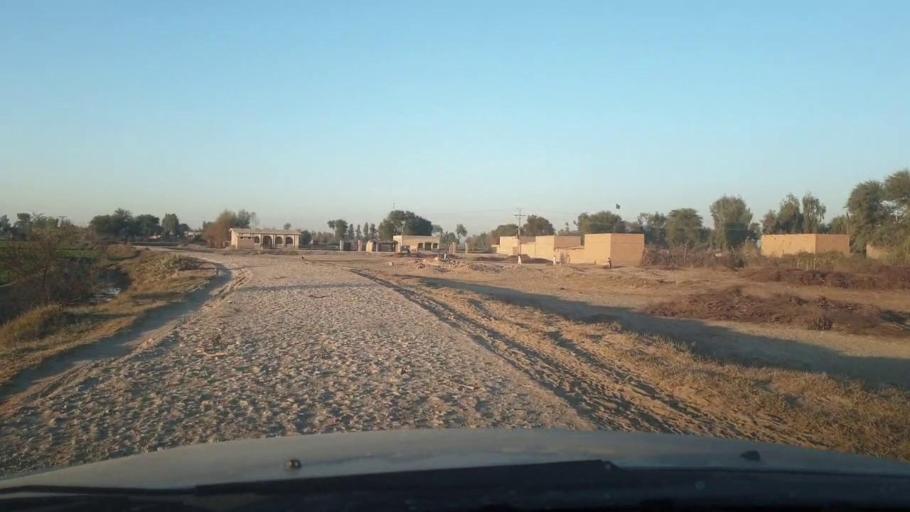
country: PK
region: Sindh
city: Pano Aqil
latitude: 27.9055
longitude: 69.1976
